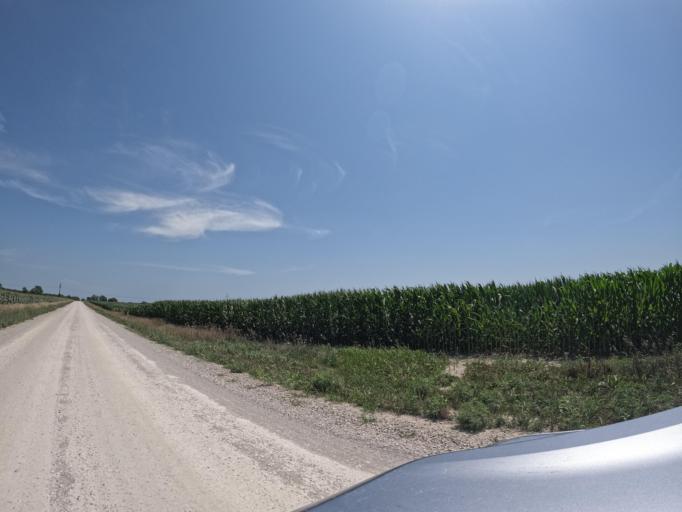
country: US
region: Iowa
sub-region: Henry County
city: Mount Pleasant
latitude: 40.9084
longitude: -91.6452
